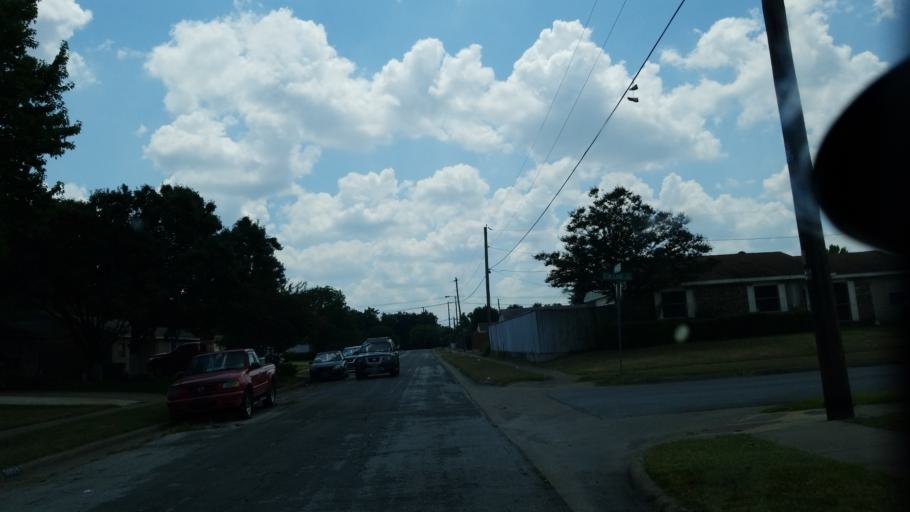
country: US
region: Texas
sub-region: Dallas County
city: Duncanville
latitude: 32.6784
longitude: -96.9003
